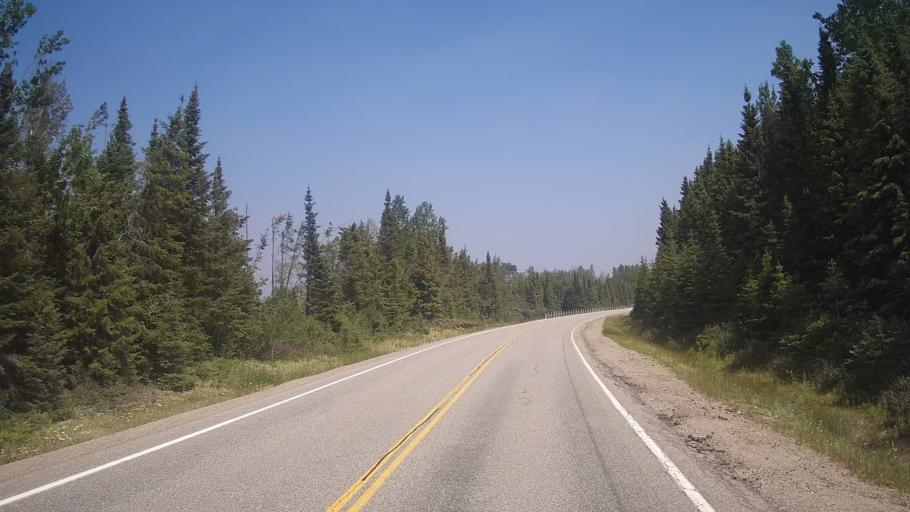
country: CA
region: Ontario
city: Timmins
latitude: 48.0514
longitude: -81.5831
